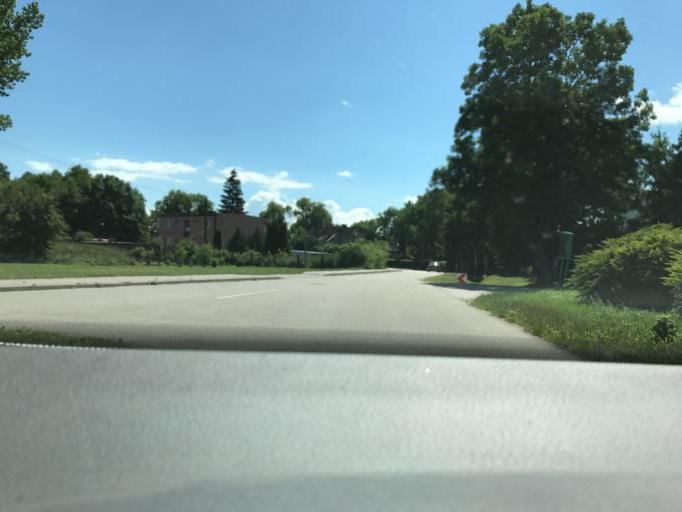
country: PL
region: Pomeranian Voivodeship
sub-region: Gdansk
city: Gdansk
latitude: 54.3306
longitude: 18.7283
